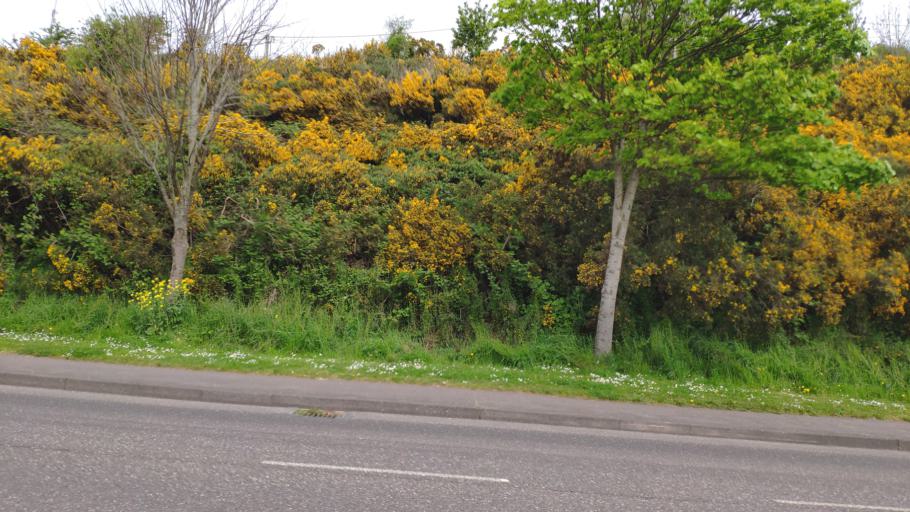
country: IE
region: Munster
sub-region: County Cork
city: Cork
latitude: 51.9148
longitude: -8.4607
